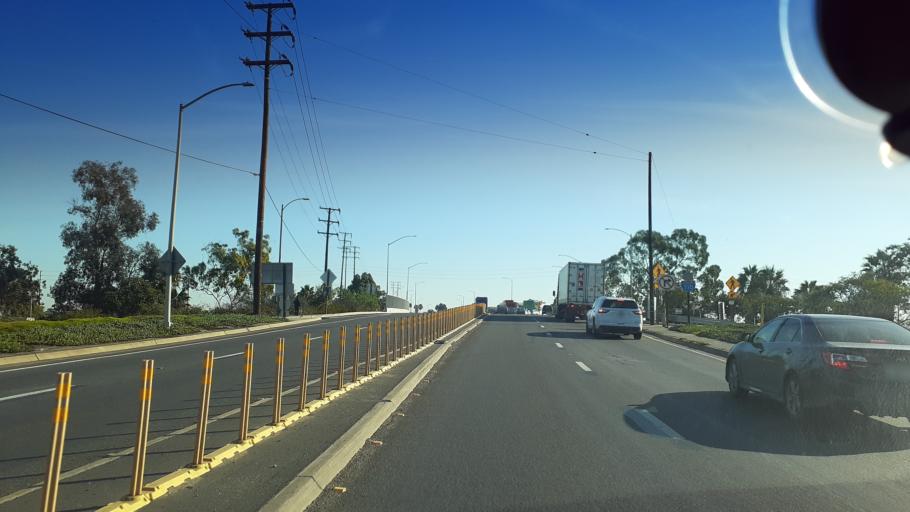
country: US
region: California
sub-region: Los Angeles County
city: Long Beach
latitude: 33.7898
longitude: -118.2105
